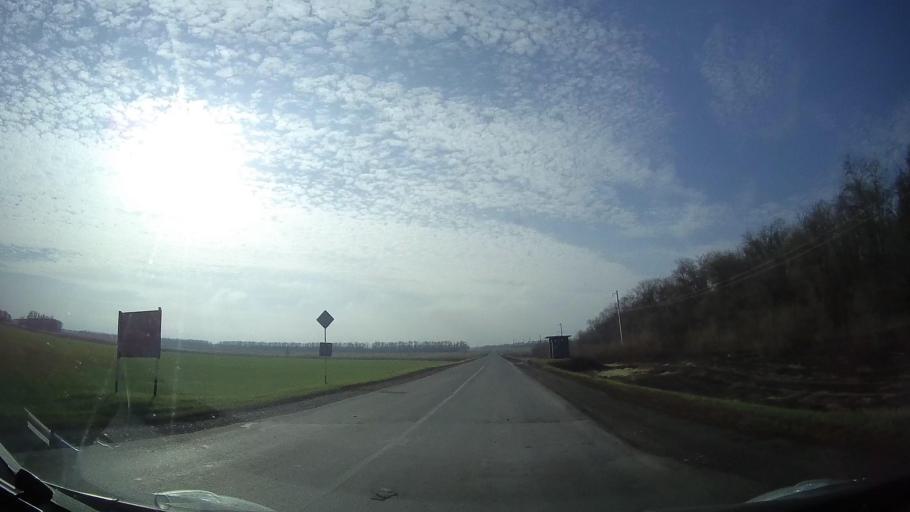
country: RU
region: Rostov
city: Mechetinskaya
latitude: 46.8137
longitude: 40.5462
